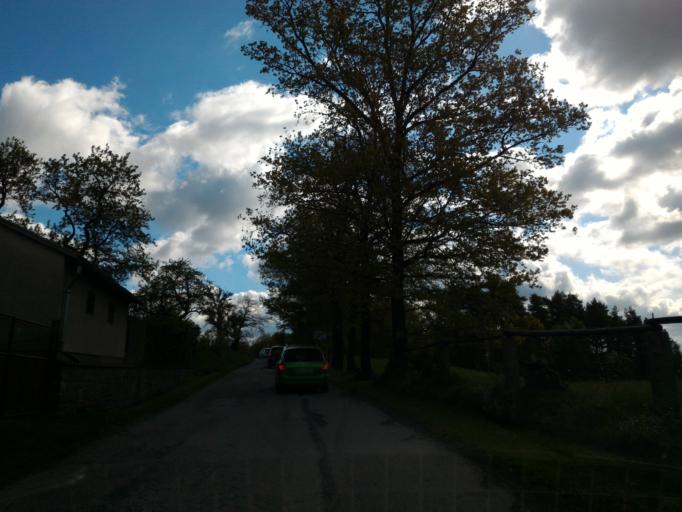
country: CZ
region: Vysocina
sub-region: Okres Pelhrimov
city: Humpolec
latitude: 49.6203
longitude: 15.3277
